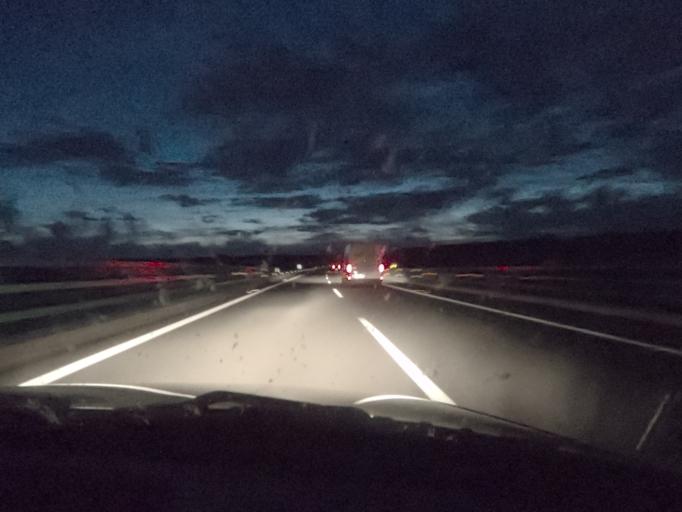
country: ES
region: Extremadura
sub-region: Provincia de Caceres
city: Morcillo
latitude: 39.9821
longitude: -6.4168
